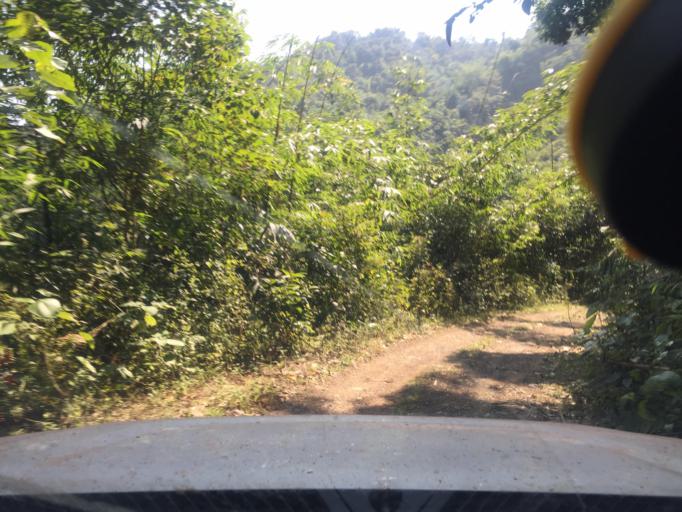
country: LA
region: Phongsali
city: Phongsali
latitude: 21.7049
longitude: 102.3965
